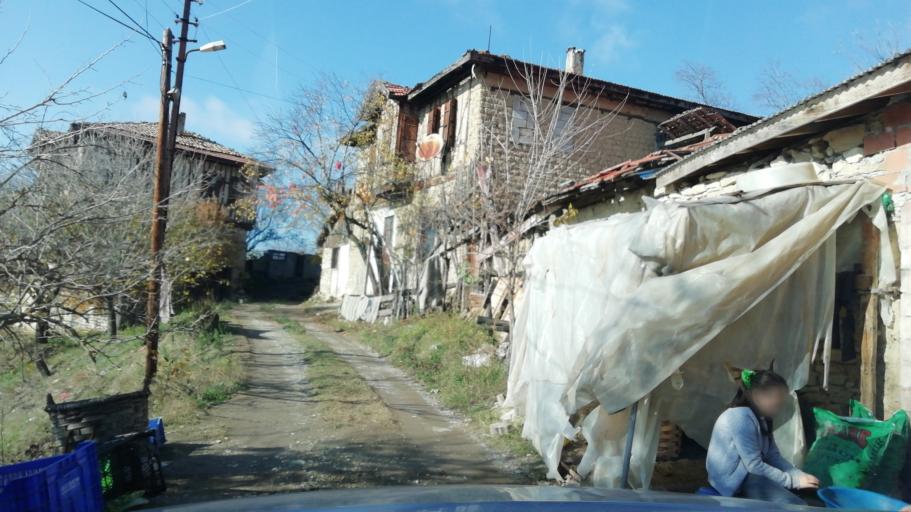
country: TR
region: Karabuk
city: Safranbolu
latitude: 41.2335
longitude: 32.7824
